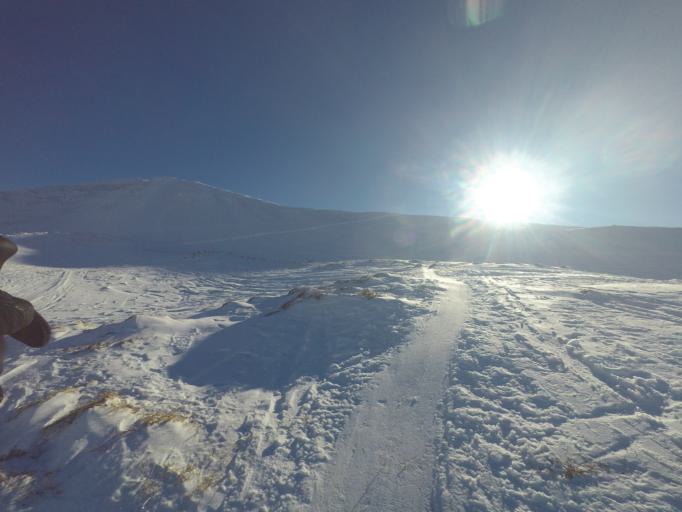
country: AT
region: Salzburg
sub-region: Politischer Bezirk Sankt Johann im Pongau
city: Huttschlag
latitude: 47.1741
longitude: 13.3038
